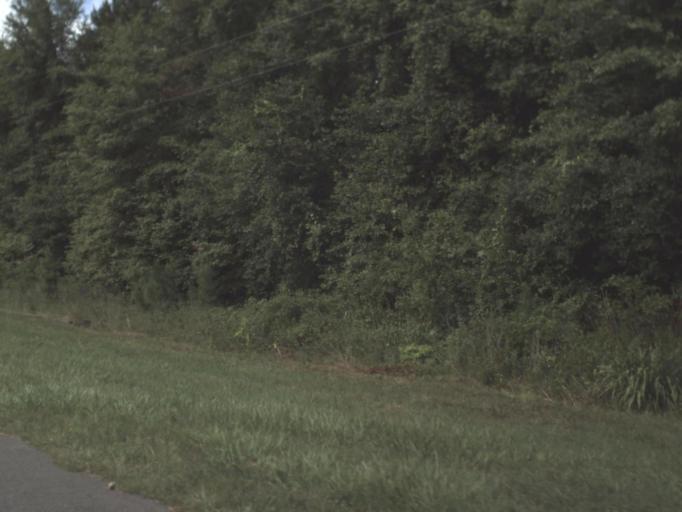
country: US
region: Florida
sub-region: Columbia County
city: Five Points
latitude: 30.3706
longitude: -82.6219
